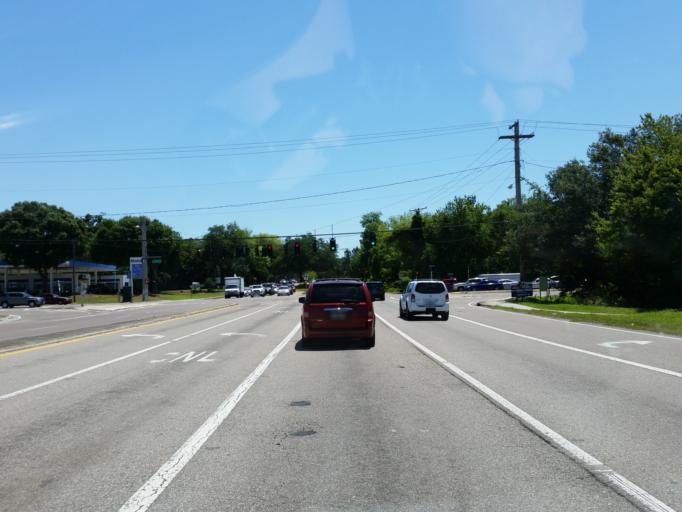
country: US
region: Florida
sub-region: Hillsborough County
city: Brandon
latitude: 27.9232
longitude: -82.2948
